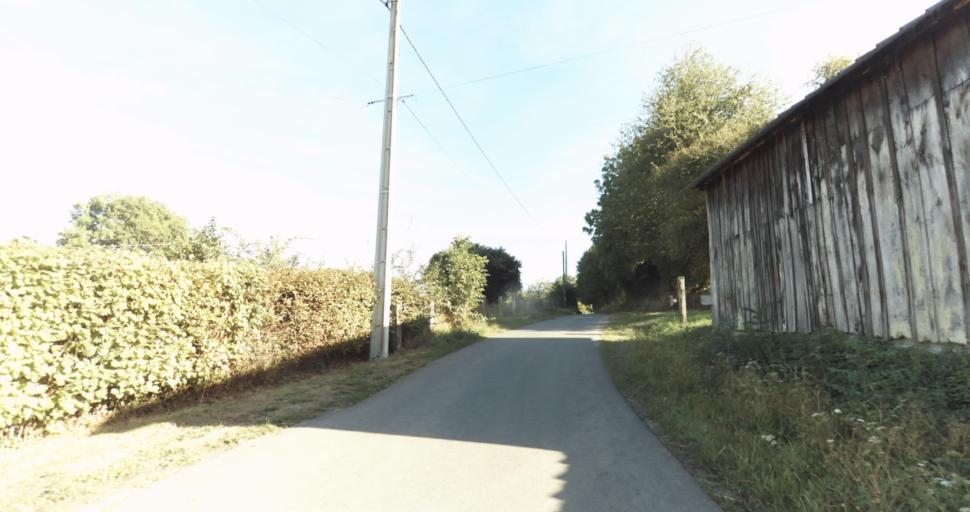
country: FR
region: Lower Normandy
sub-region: Departement de l'Orne
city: Vimoutiers
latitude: 48.9104
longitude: 0.1285
